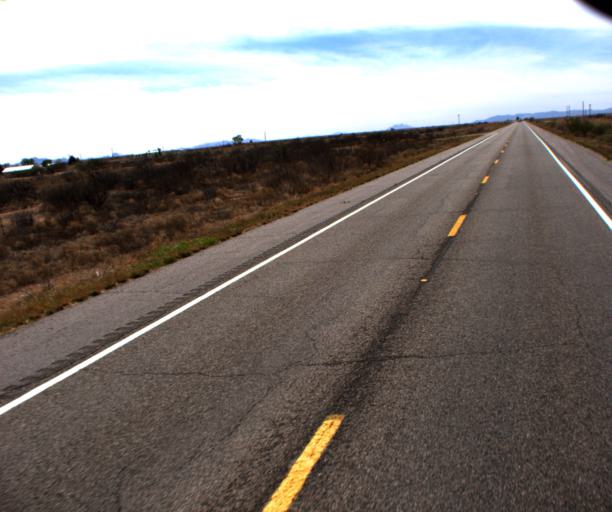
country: US
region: Arizona
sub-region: Cochise County
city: Pirtleville
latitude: 31.5731
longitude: -109.6682
